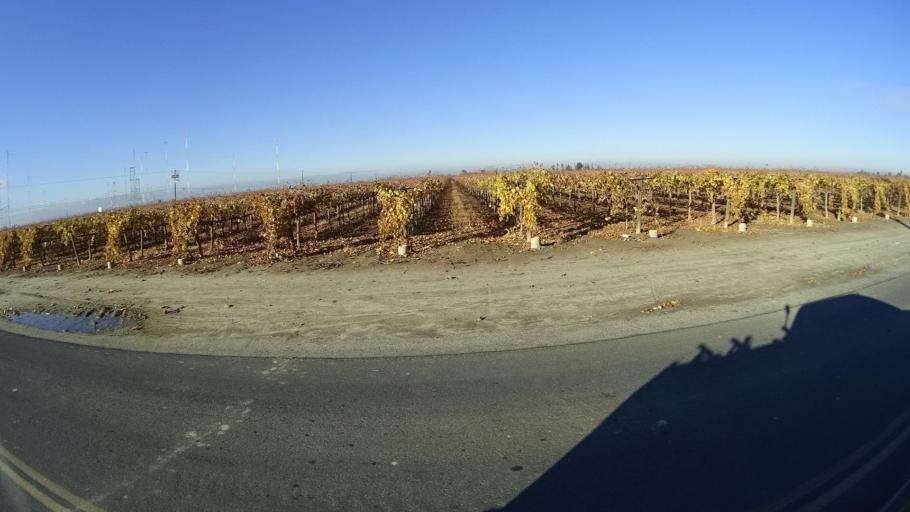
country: US
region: California
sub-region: Kern County
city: Delano
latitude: 35.7619
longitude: -119.2762
